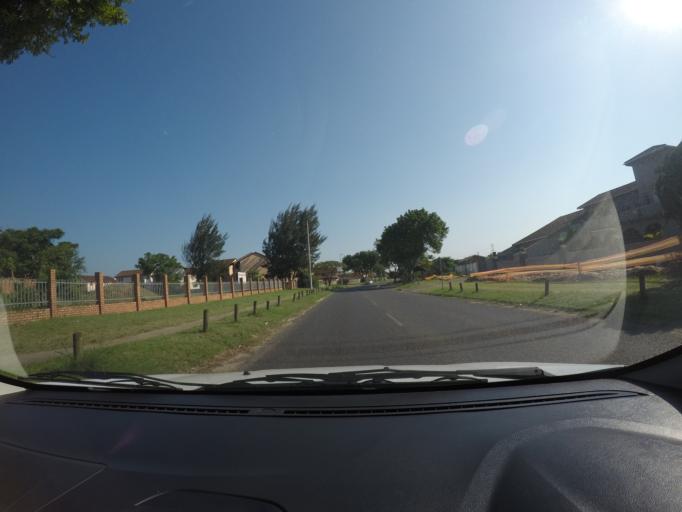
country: ZA
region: KwaZulu-Natal
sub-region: uThungulu District Municipality
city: Richards Bay
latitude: -28.7277
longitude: 32.0420
